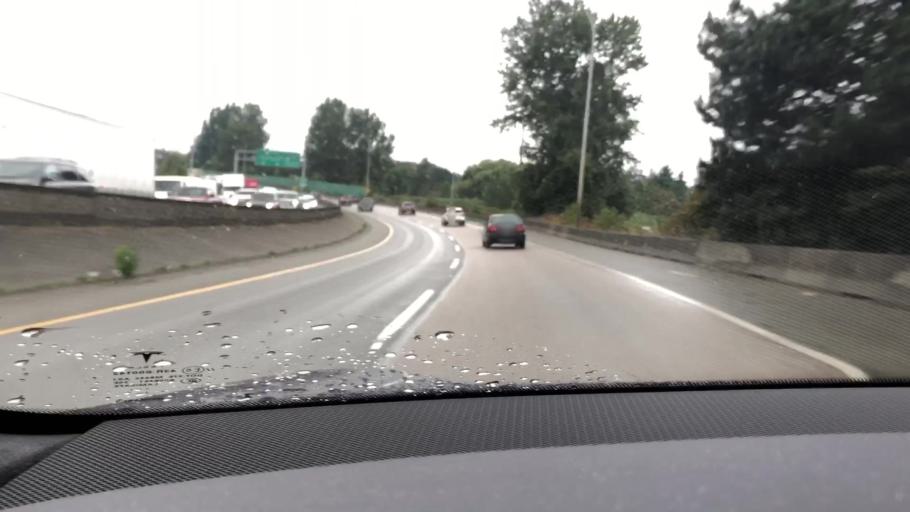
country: CA
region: British Columbia
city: New Westminster
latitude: 49.1817
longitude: -122.9592
